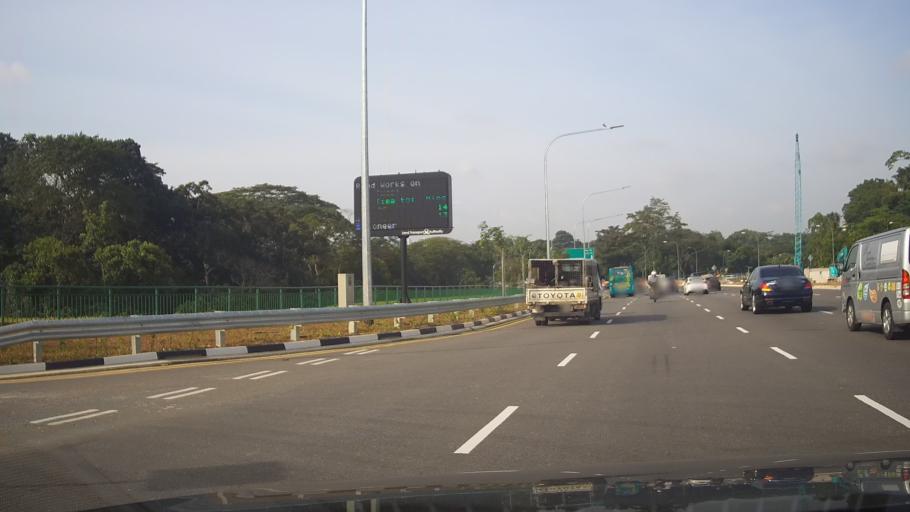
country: SG
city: Singapore
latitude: 1.3347
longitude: 103.8193
